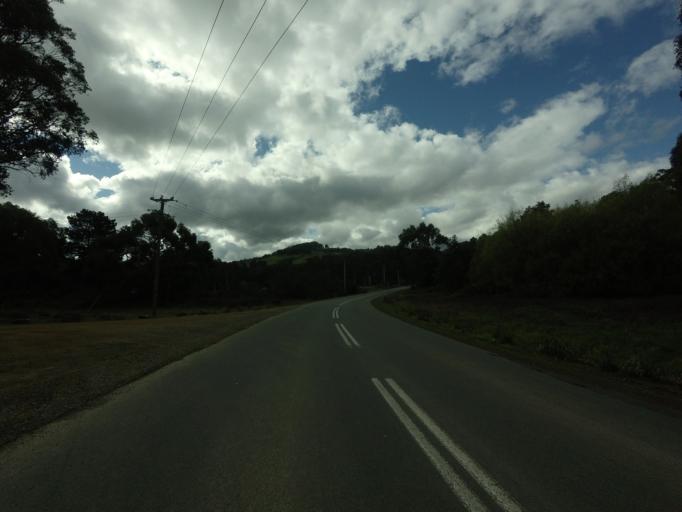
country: AU
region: Tasmania
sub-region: Huon Valley
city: Geeveston
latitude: -43.1682
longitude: 146.9406
